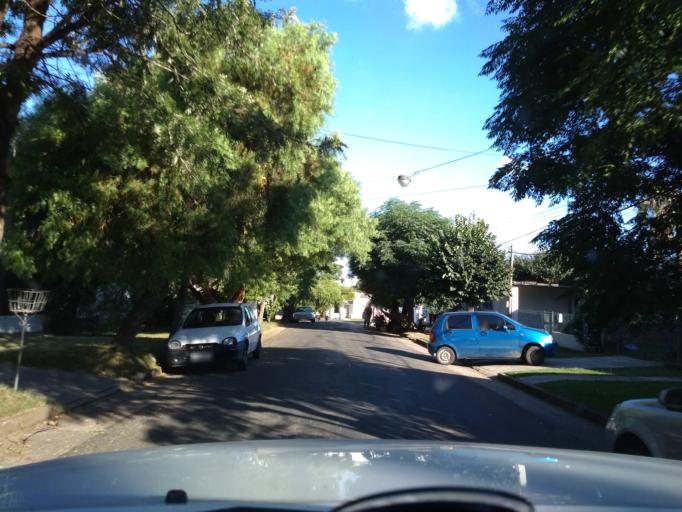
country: UY
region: Florida
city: Florida
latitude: -34.0973
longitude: -56.2264
